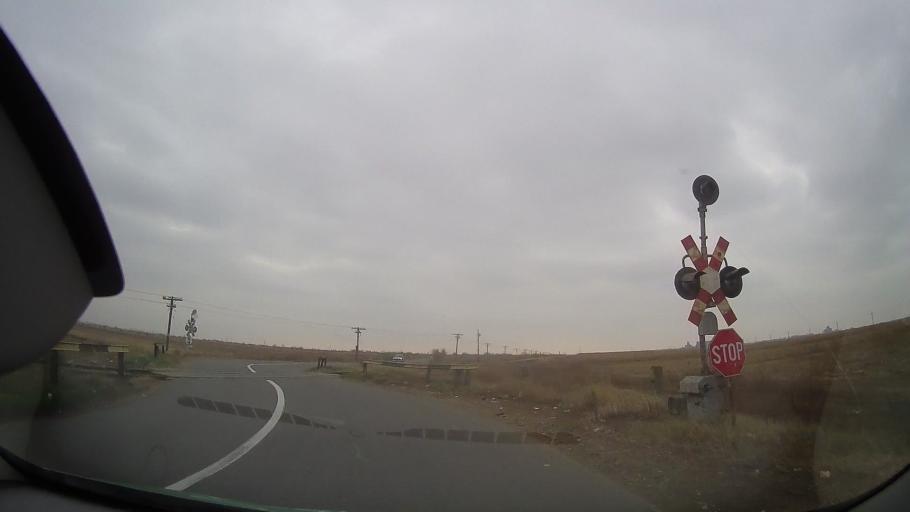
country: RO
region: Ialomita
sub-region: Comuna Manasia
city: Manasia
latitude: 44.7237
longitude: 26.6899
